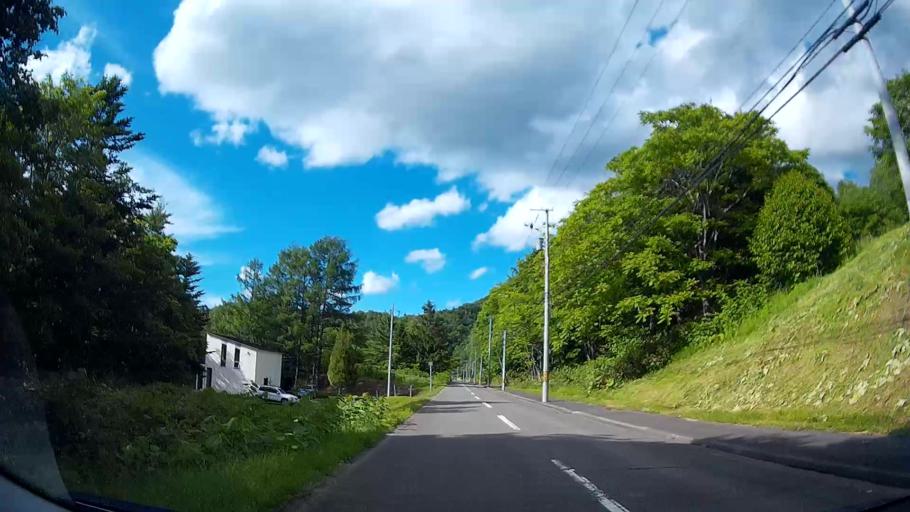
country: JP
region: Hokkaido
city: Sapporo
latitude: 42.9456
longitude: 141.1544
